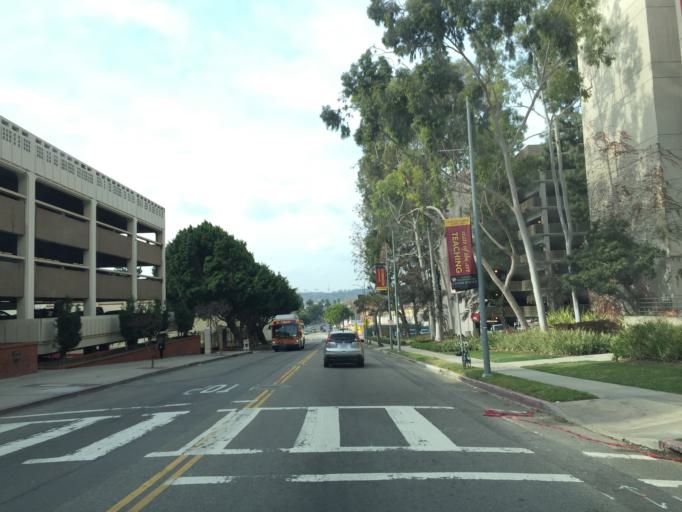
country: US
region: California
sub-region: Los Angeles County
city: Boyle Heights
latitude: 34.0600
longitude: -118.2059
